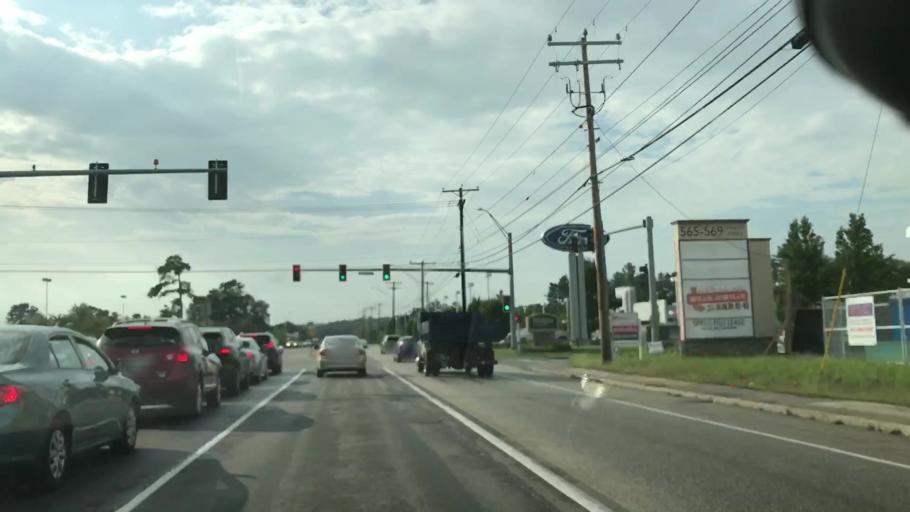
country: US
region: New Hampshire
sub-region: Hillsborough County
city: Litchfield
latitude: 42.7987
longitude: -71.5329
